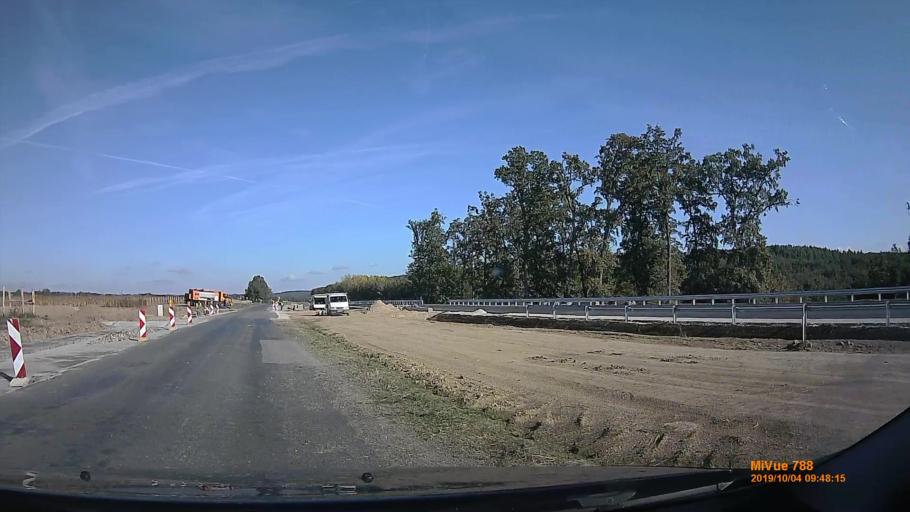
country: HU
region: Somogy
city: Kaposvar
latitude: 46.4370
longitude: 17.7709
